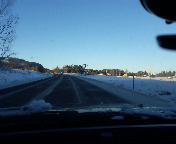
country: SE
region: Gaevleborg
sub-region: Bollnas Kommun
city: Arbra
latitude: 61.5354
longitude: 16.3632
